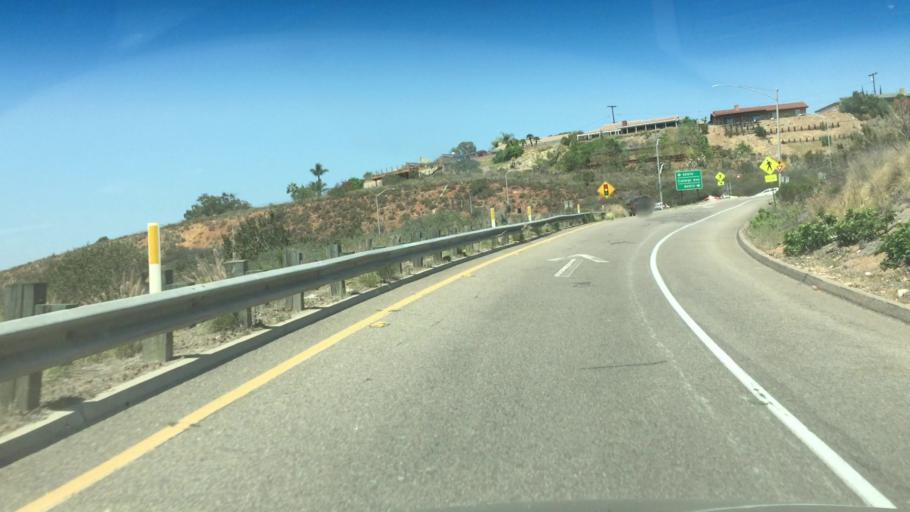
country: US
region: California
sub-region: San Diego County
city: La Mesa
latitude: 32.7799
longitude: -117.0641
